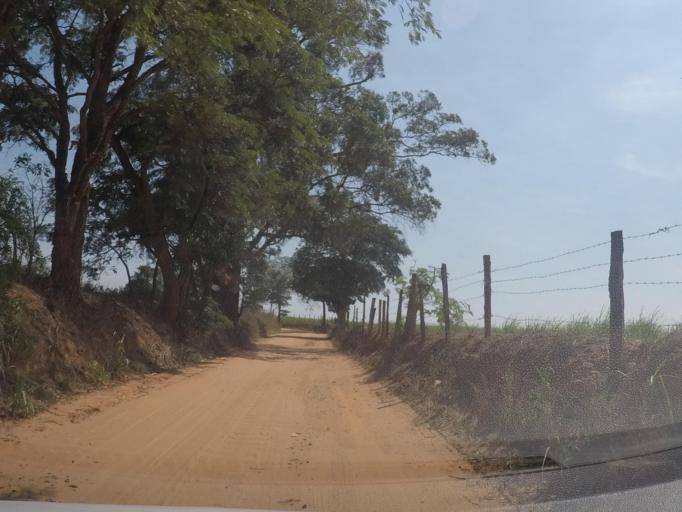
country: BR
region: Sao Paulo
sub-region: Sumare
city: Sumare
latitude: -22.8754
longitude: -47.2875
